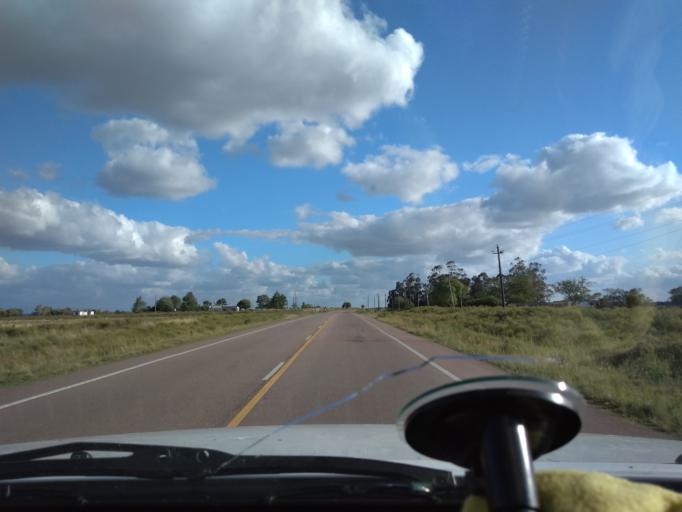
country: UY
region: Canelones
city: Tala
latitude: -34.4043
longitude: -55.8014
